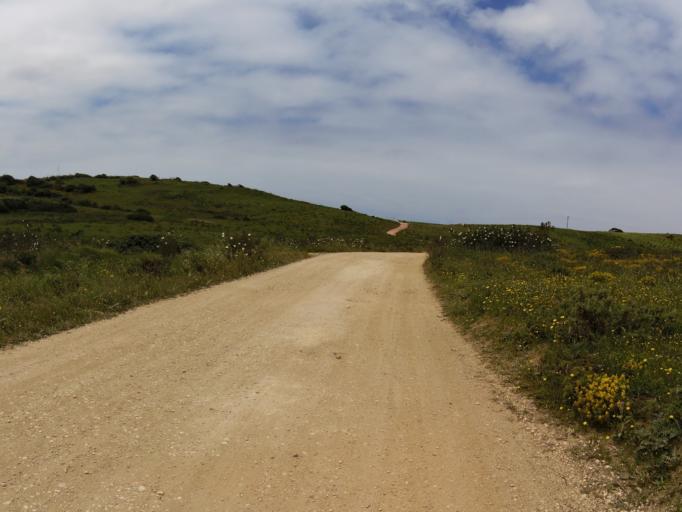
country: PT
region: Faro
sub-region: Vila do Bispo
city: Vila do Bispo
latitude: 37.0873
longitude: -8.8973
